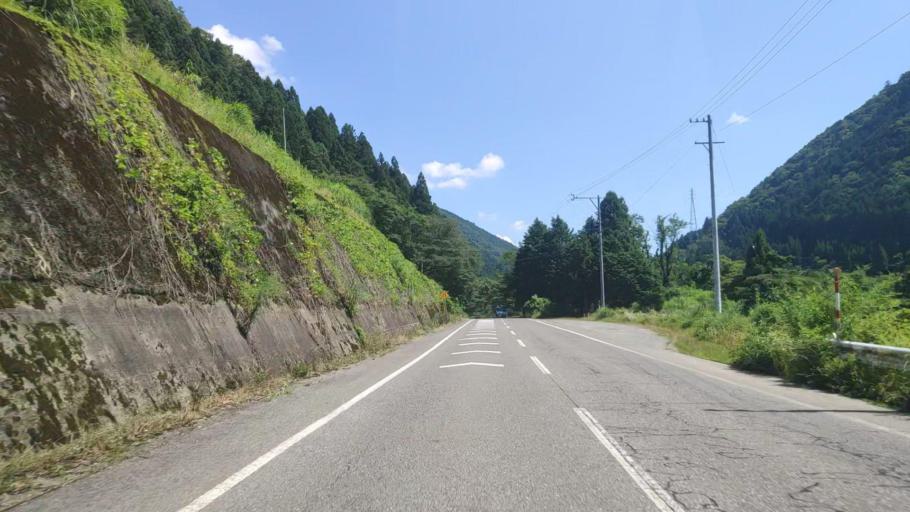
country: JP
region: Gifu
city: Godo
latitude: 35.6138
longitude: 136.6246
